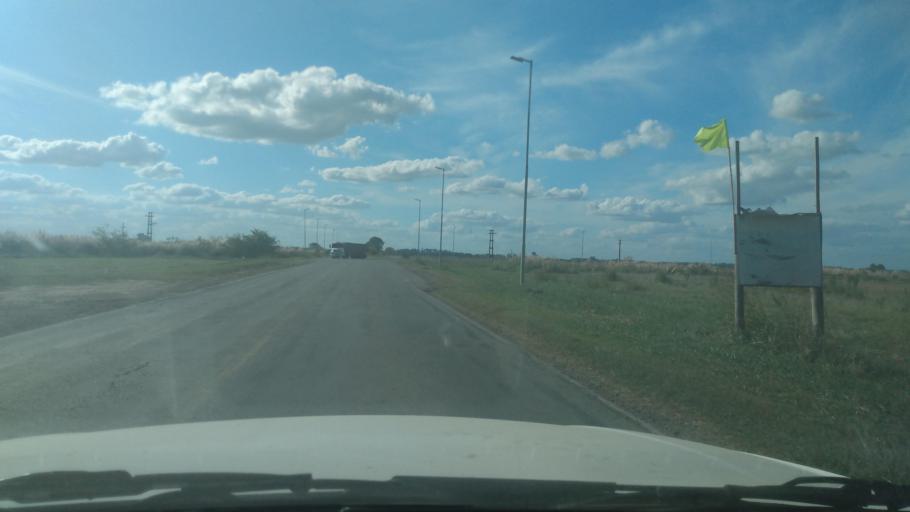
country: AR
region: Buenos Aires
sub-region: Partido de Navarro
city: Navarro
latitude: -34.9875
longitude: -59.3153
